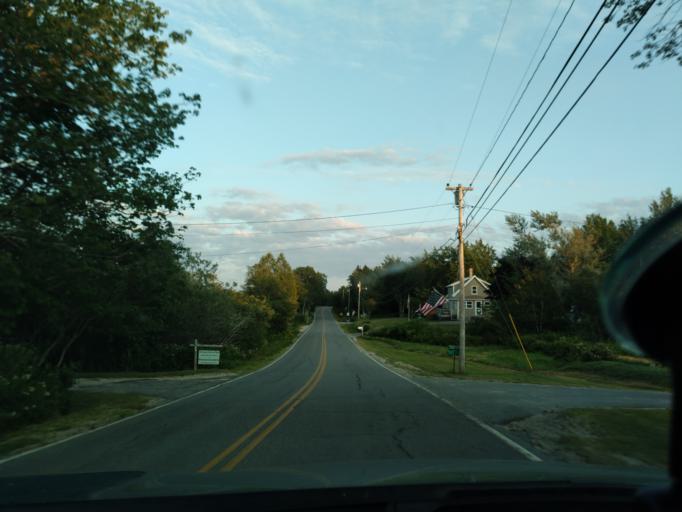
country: US
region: Maine
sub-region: Hancock County
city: Gouldsboro
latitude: 44.3863
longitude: -68.0391
